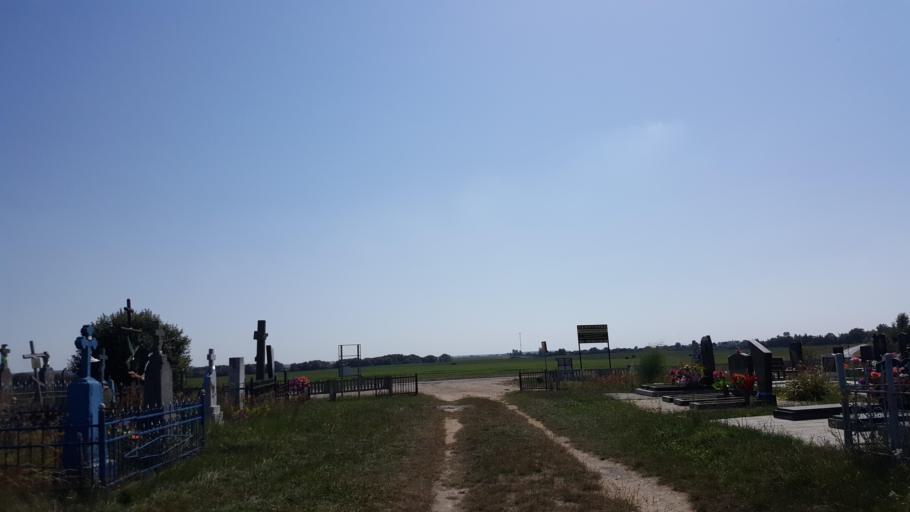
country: PL
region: Podlasie
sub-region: Powiat hajnowski
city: Czeremcha
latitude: 52.4789
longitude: 23.5201
